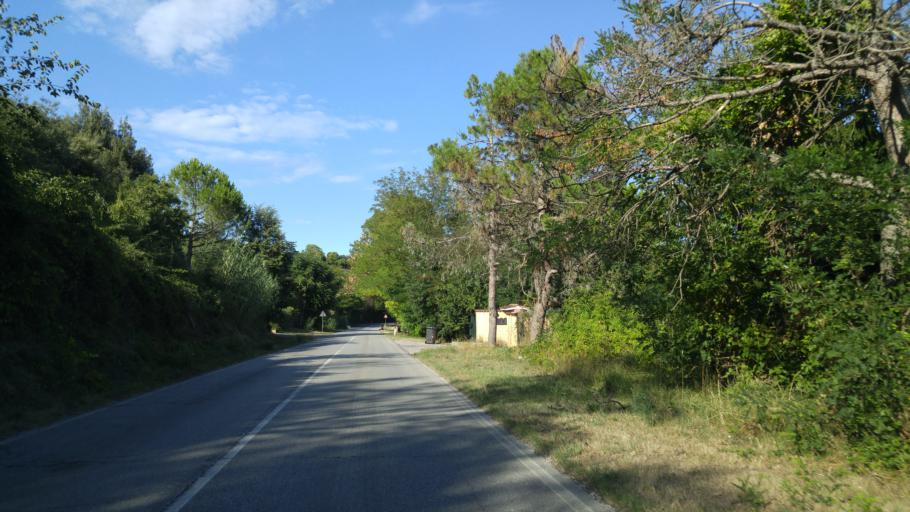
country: IT
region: The Marches
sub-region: Provincia di Pesaro e Urbino
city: Pesaro
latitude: 43.8697
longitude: 12.8837
